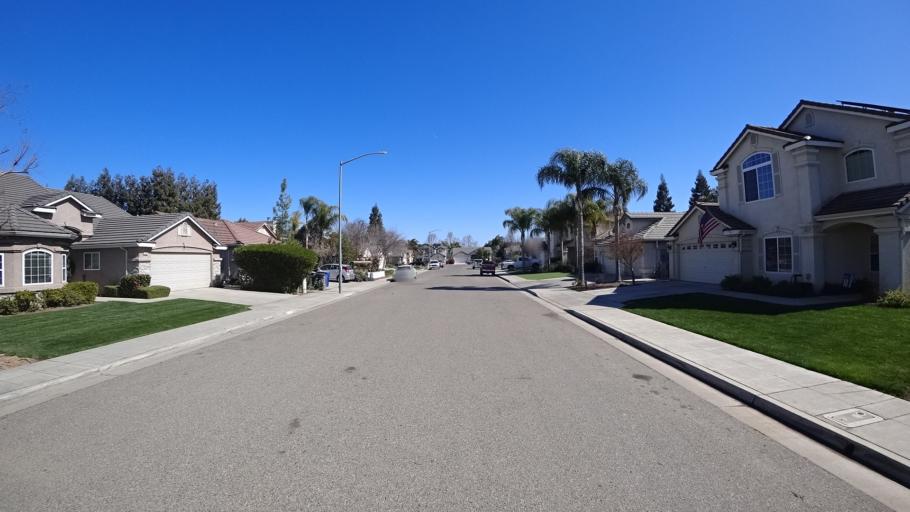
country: US
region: California
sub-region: Fresno County
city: Clovis
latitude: 36.8753
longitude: -119.7322
